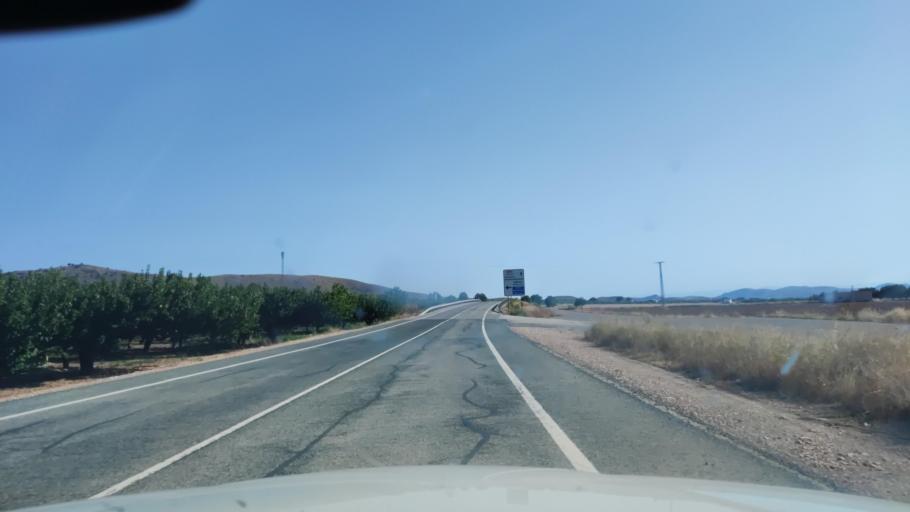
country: ES
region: Castille-La Mancha
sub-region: Provincia de Albacete
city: Tobarra
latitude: 38.6369
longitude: -1.6678
